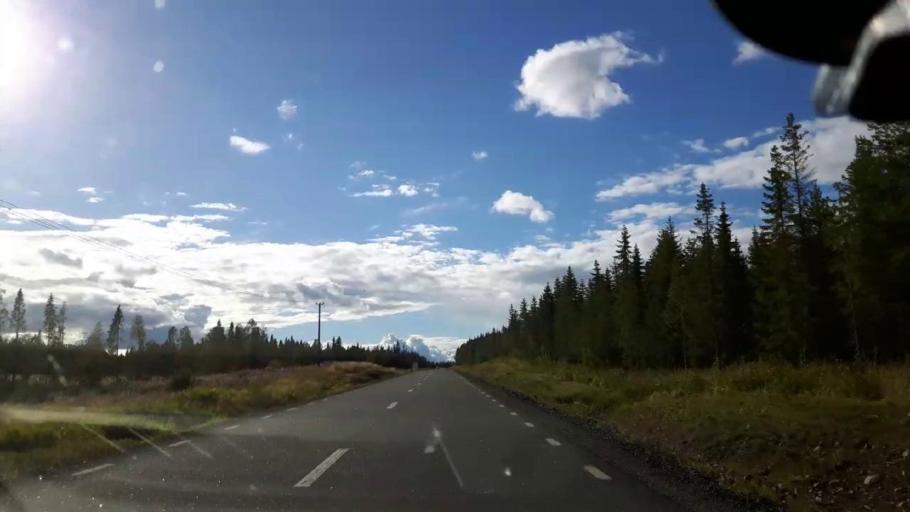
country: SE
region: Jaemtland
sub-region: Stroemsunds Kommun
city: Stroemsund
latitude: 63.5426
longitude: 15.9336
